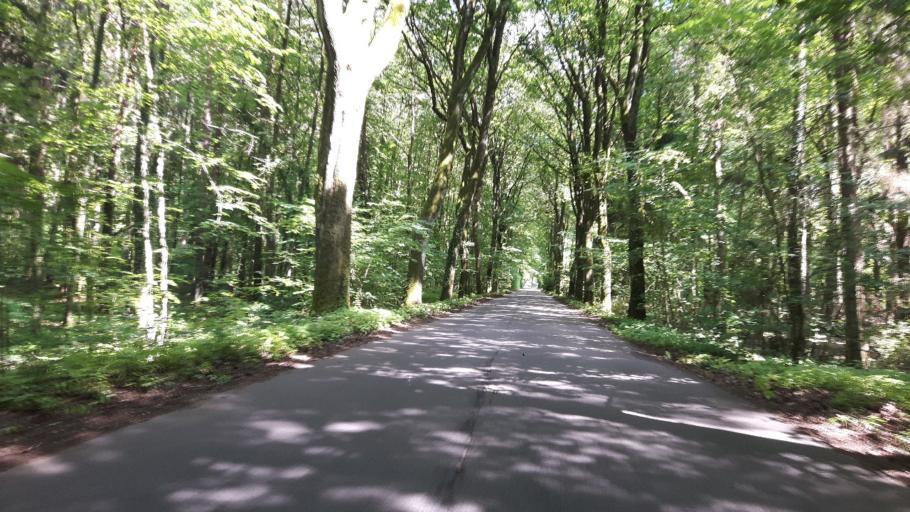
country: PL
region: West Pomeranian Voivodeship
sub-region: Powiat goleniowski
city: Nowogard
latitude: 53.6707
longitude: 15.0889
